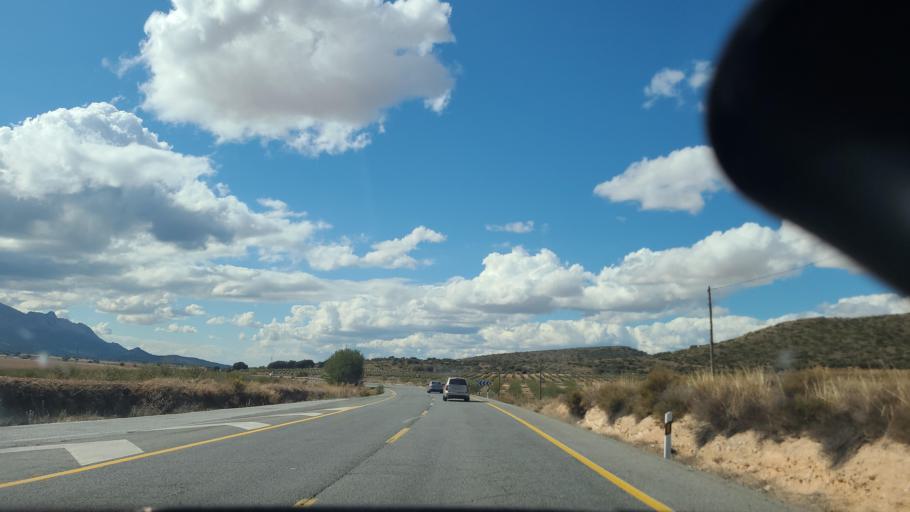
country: ES
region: Andalusia
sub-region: Provincia de Granada
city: Pinar
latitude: 37.4058
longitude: -3.3897
